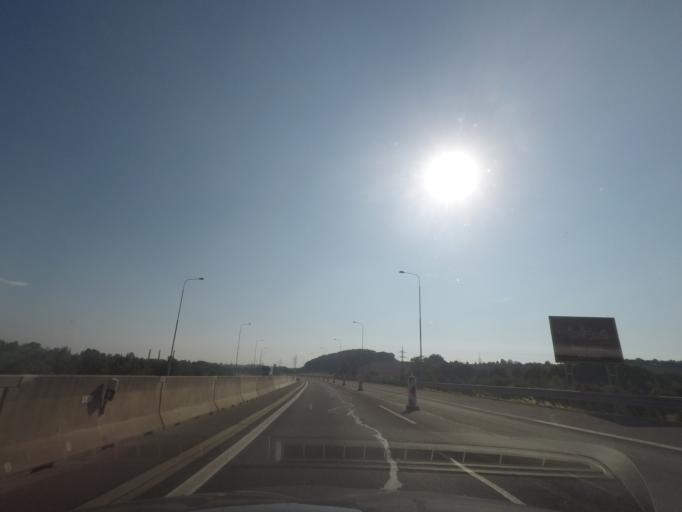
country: CZ
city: Ludgerovice
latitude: 49.8496
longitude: 18.2305
